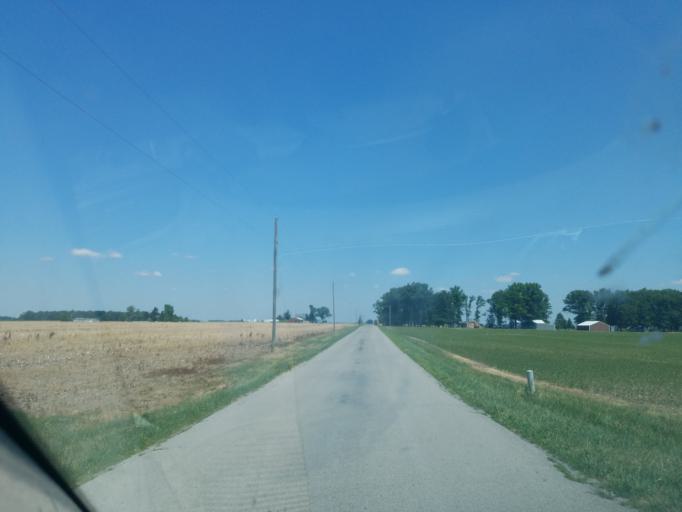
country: US
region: Ohio
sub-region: Allen County
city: Spencerville
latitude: 40.7528
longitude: -84.3971
